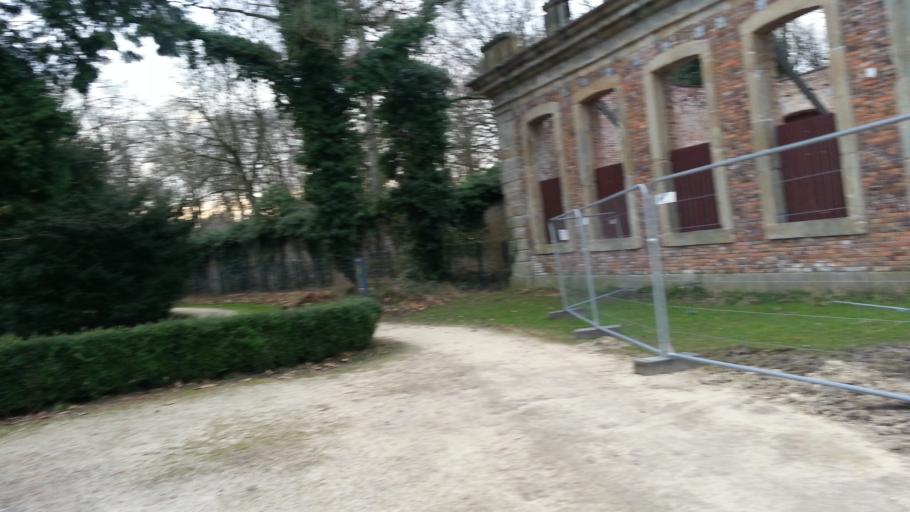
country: DE
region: North Rhine-Westphalia
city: Herten
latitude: 51.5937
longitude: 7.1304
